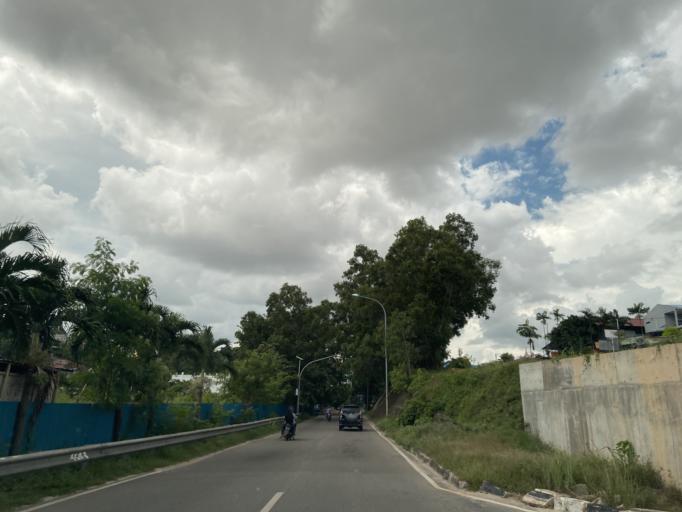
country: SG
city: Singapore
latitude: 1.1324
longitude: 104.0129
